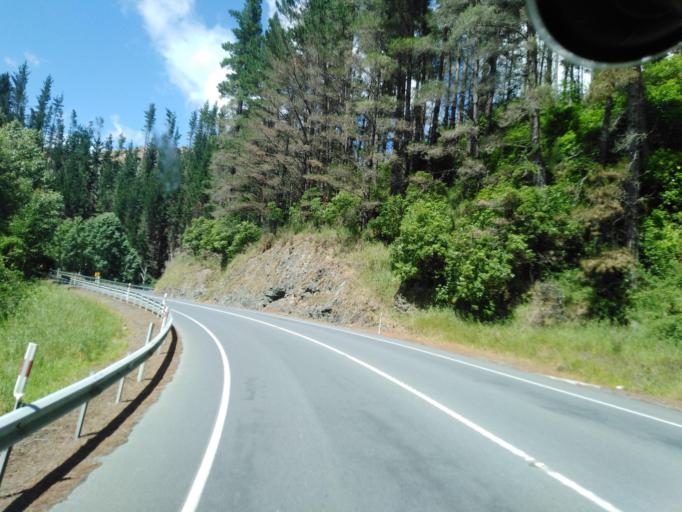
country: NZ
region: Nelson
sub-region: Nelson City
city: Nelson
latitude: -41.2284
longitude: 173.4014
